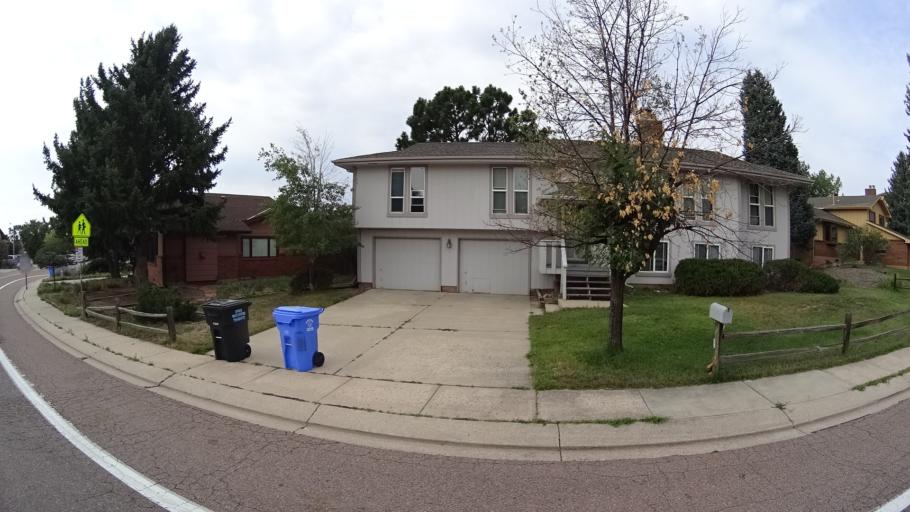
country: US
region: Colorado
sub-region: El Paso County
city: Air Force Academy
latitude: 38.9301
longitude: -104.8359
